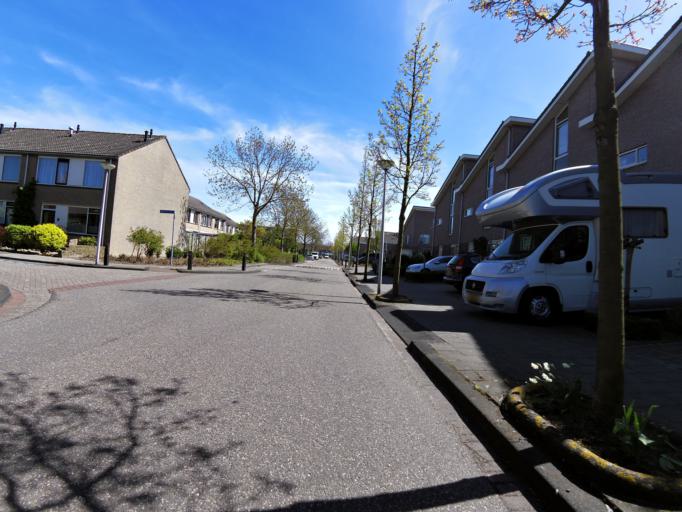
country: NL
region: South Holland
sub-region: Gemeente Brielle
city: Brielle
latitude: 51.9144
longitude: 4.1070
